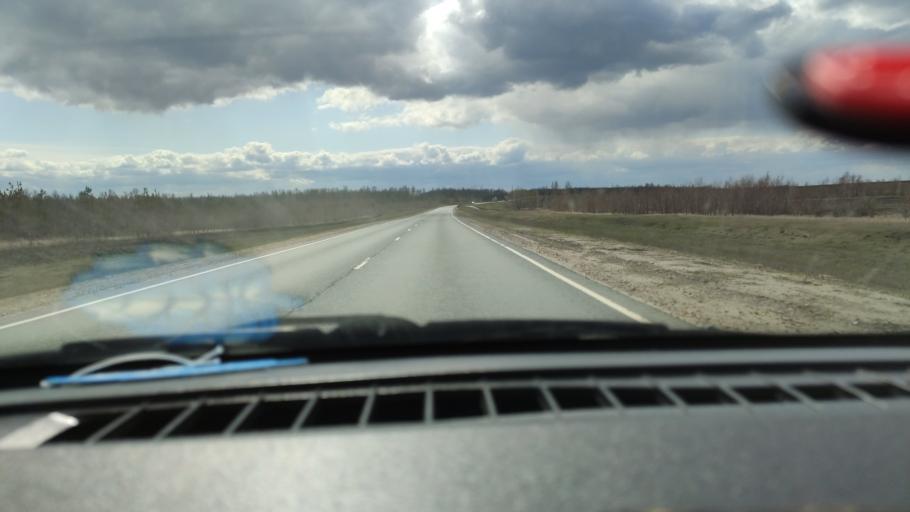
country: RU
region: Saratov
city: Alekseyevka
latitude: 52.2781
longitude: 47.9316
